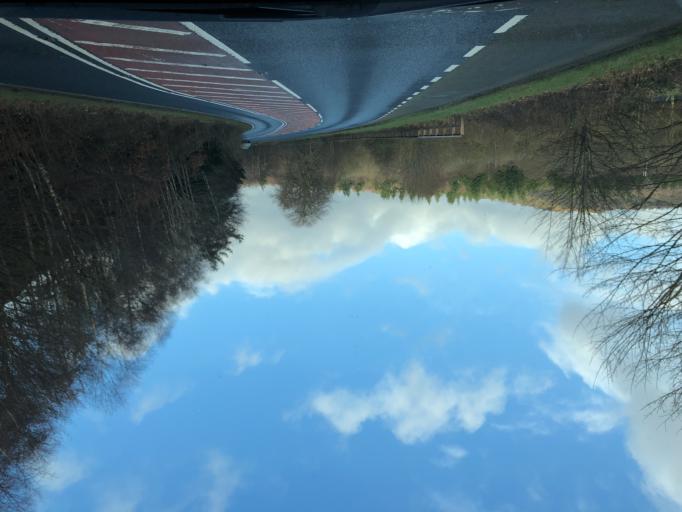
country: GB
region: England
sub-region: Cumbria
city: Grange-over-Sands
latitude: 54.2609
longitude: -2.9878
